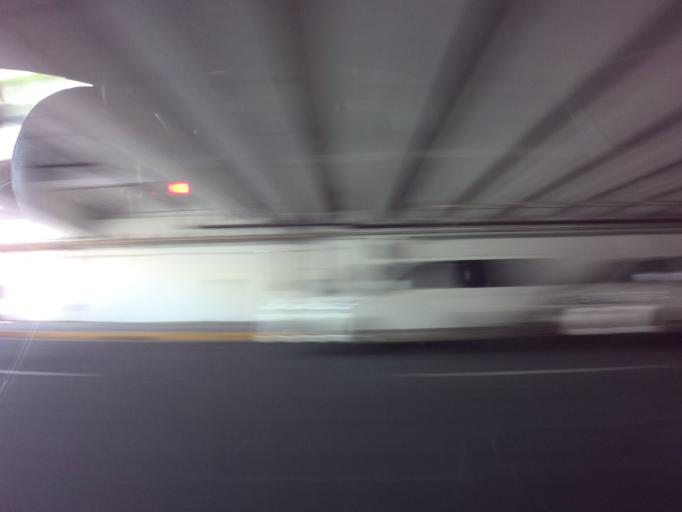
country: PH
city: Sambayanihan People's Village
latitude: 14.5139
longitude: 120.9783
